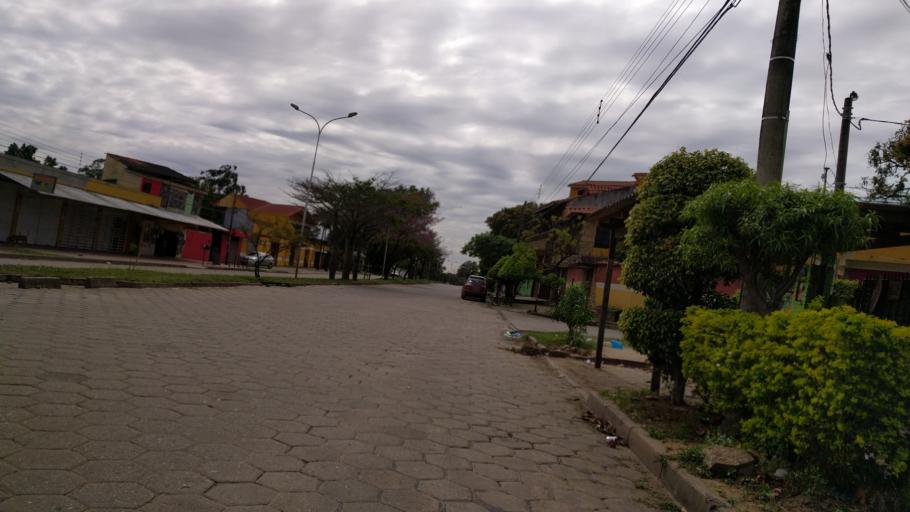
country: BO
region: Santa Cruz
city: Santa Cruz de la Sierra
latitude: -17.8156
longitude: -63.1984
